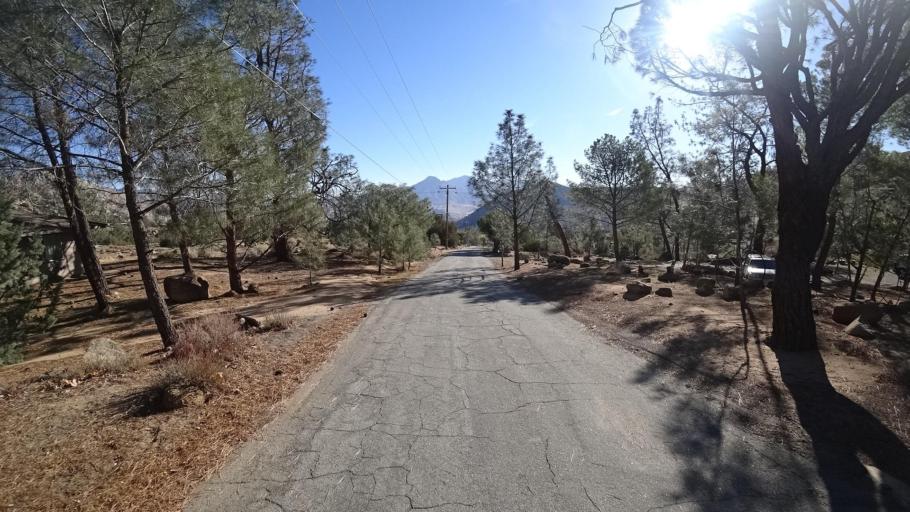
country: US
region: California
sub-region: Kern County
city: Weldon
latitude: 35.7167
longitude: -118.3056
